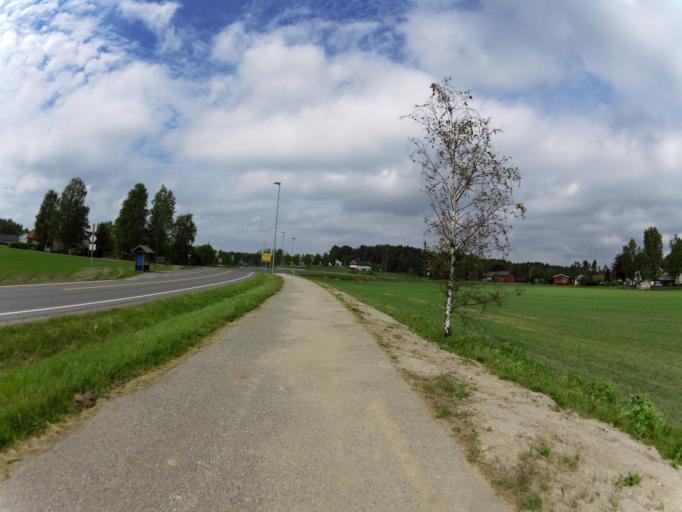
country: NO
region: Ostfold
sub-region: Rade
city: Karlshus
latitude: 59.3443
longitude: 10.9320
